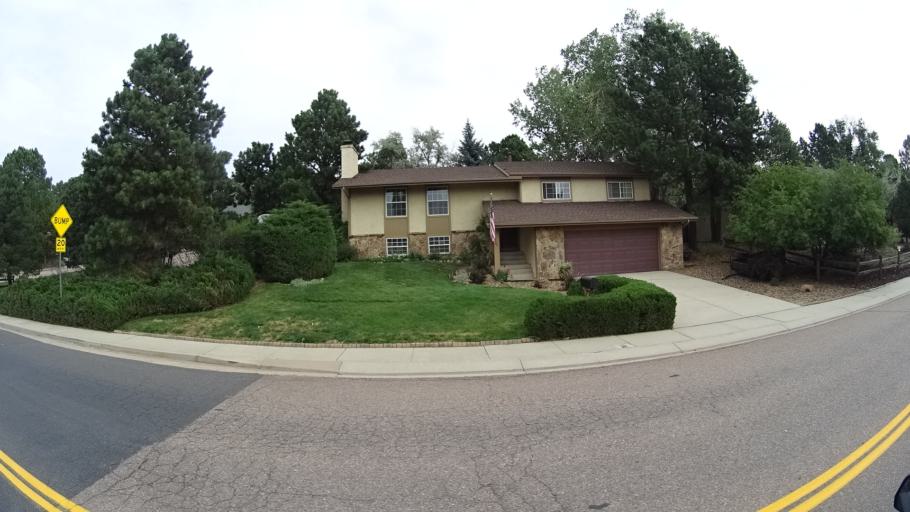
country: US
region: Colorado
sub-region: El Paso County
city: Air Force Academy
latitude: 38.9303
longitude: -104.8384
